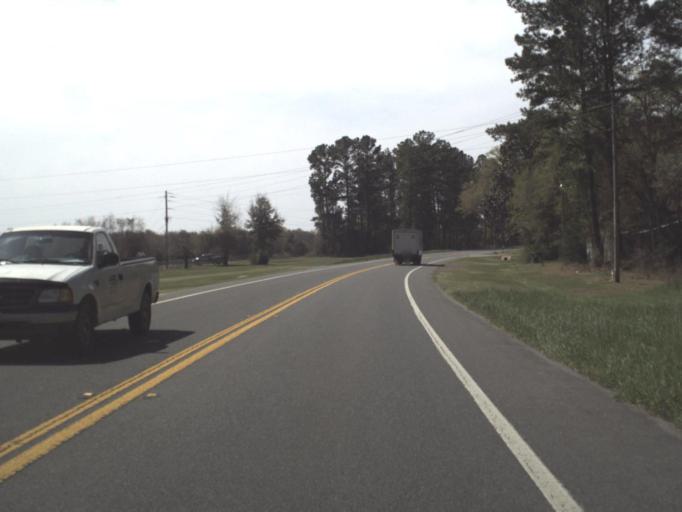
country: US
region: Florida
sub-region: Holmes County
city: Bonifay
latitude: 30.7686
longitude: -85.8521
